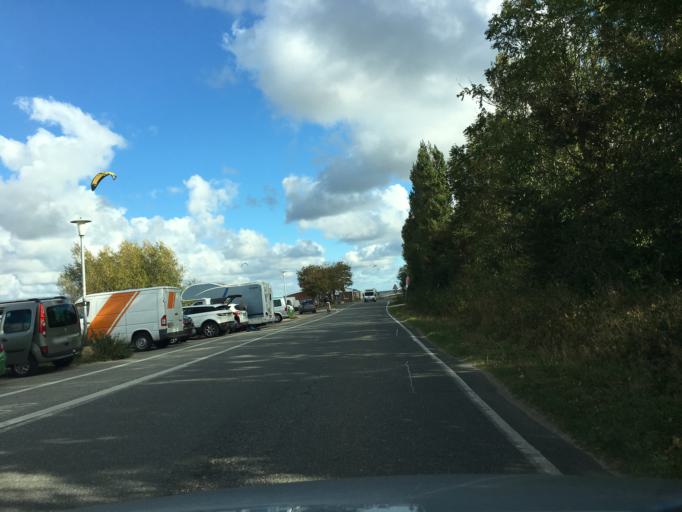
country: DE
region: Schleswig-Holstein
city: Laboe
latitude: 54.4149
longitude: 10.2394
